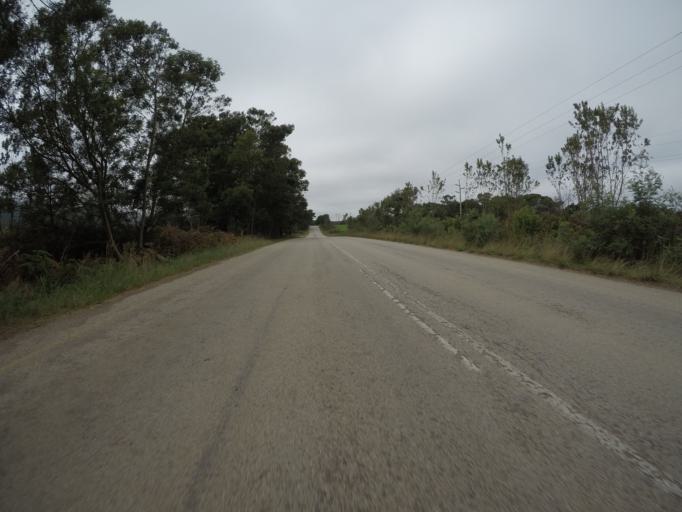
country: ZA
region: Eastern Cape
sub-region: Cacadu District Municipality
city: Kareedouw
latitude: -33.9967
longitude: 24.1479
